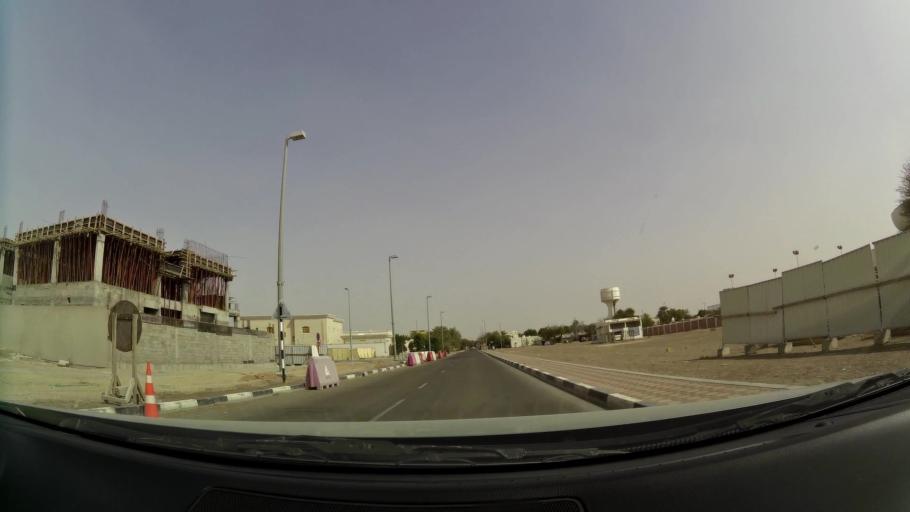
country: AE
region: Abu Dhabi
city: Al Ain
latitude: 24.1873
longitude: 55.6227
